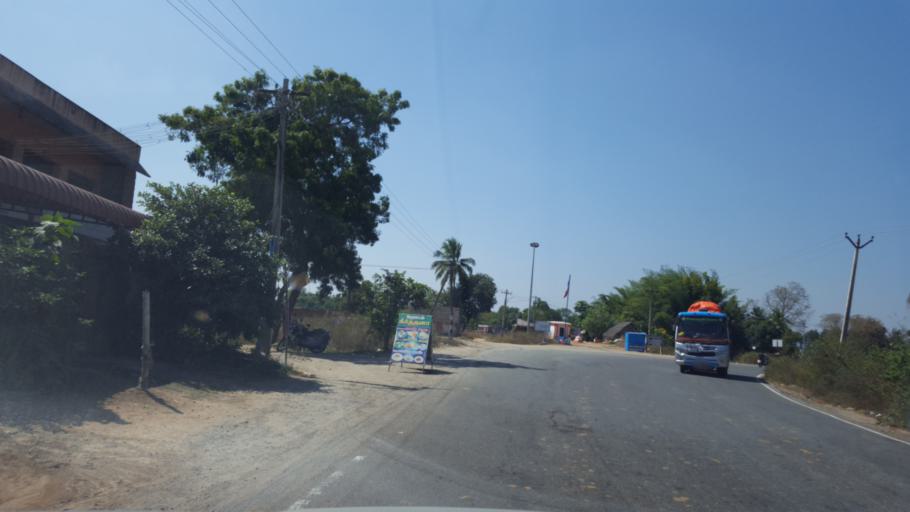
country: IN
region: Tamil Nadu
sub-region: Kancheepuram
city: Wallajahbad
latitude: 12.7629
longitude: 79.9098
